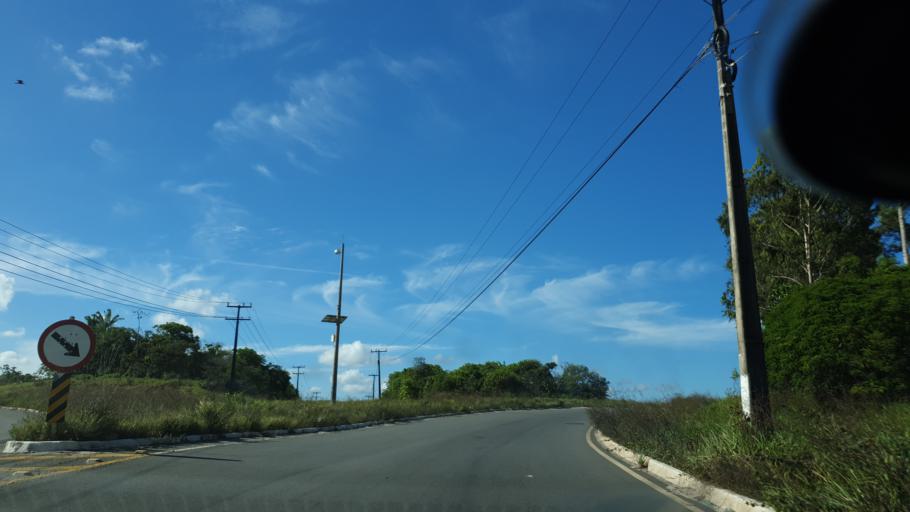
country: BR
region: Bahia
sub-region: Camacari
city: Camacari
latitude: -12.6814
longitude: -38.2815
